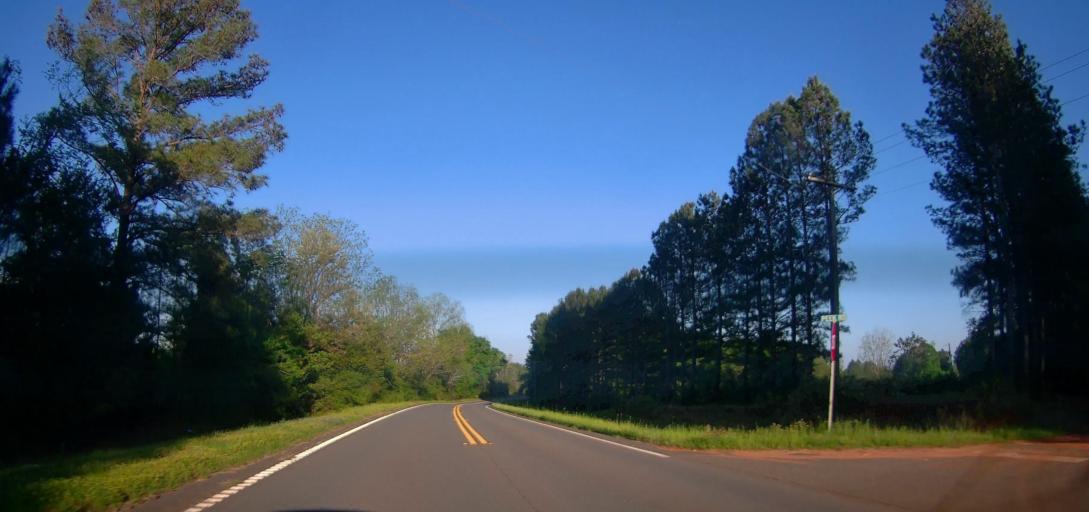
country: US
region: Georgia
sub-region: Schley County
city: Ellaville
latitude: 32.3198
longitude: -84.2625
